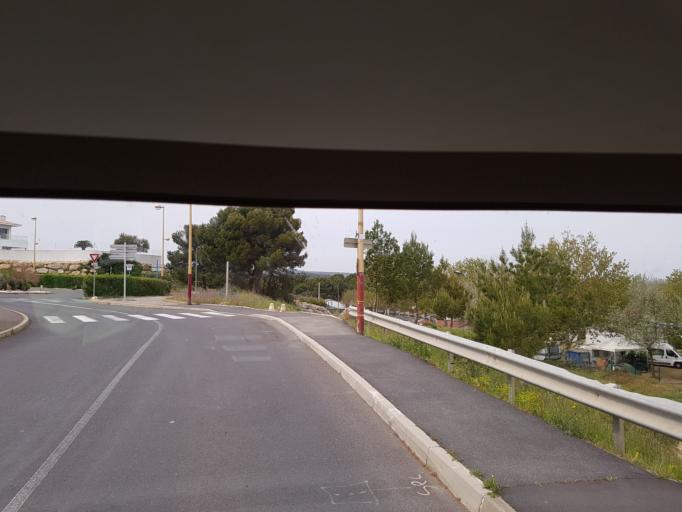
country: FR
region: Languedoc-Roussillon
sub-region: Departement de l'Aude
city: Fleury
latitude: 43.1880
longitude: 3.1972
